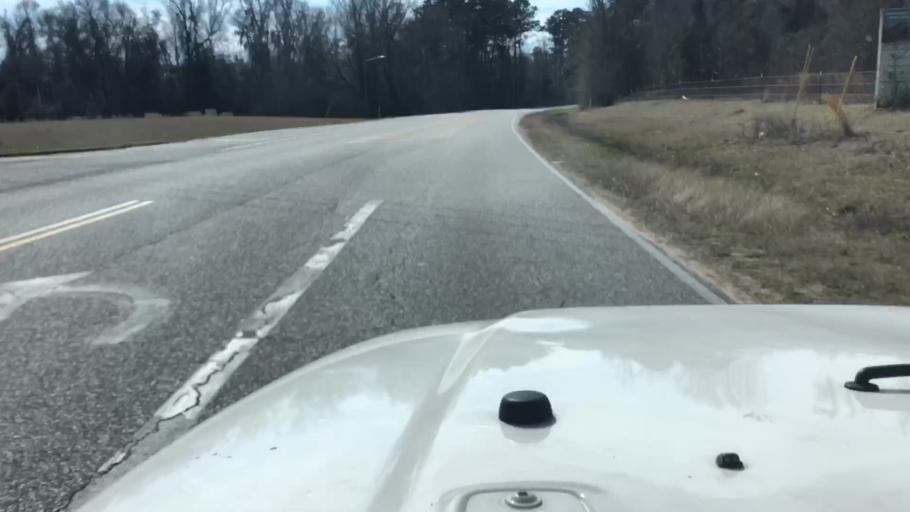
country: US
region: Alabama
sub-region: Elmore County
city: Blue Ridge
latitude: 32.3976
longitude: -86.1668
